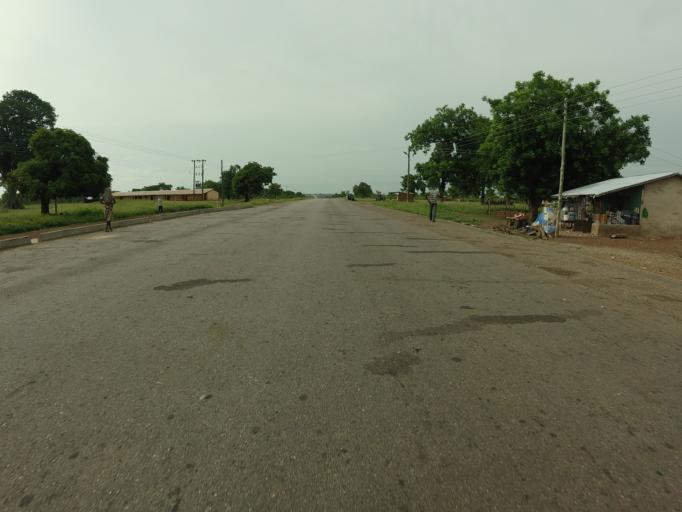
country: GH
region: Northern
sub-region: Yendi
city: Yendi
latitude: 9.6387
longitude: -0.0639
